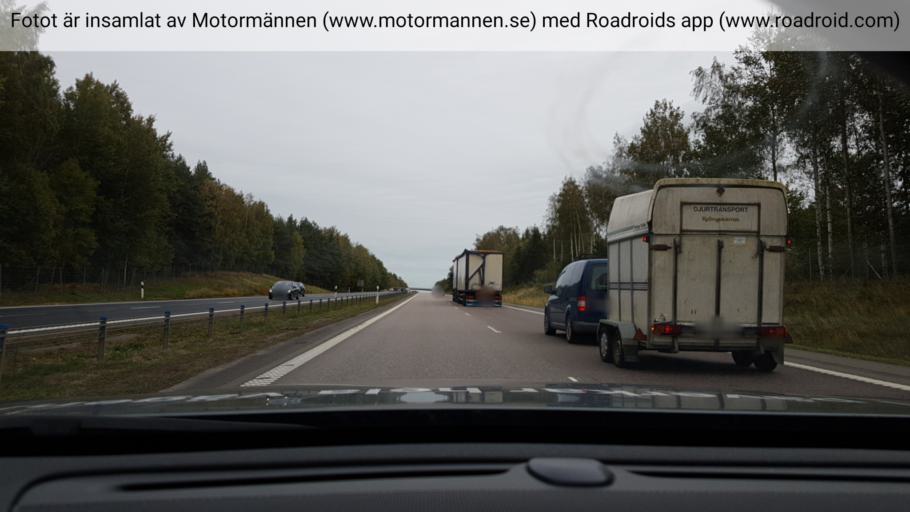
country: SE
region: OEstergoetland
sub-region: Mjolby Kommun
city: Mantorp
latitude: 58.3793
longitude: 15.3425
